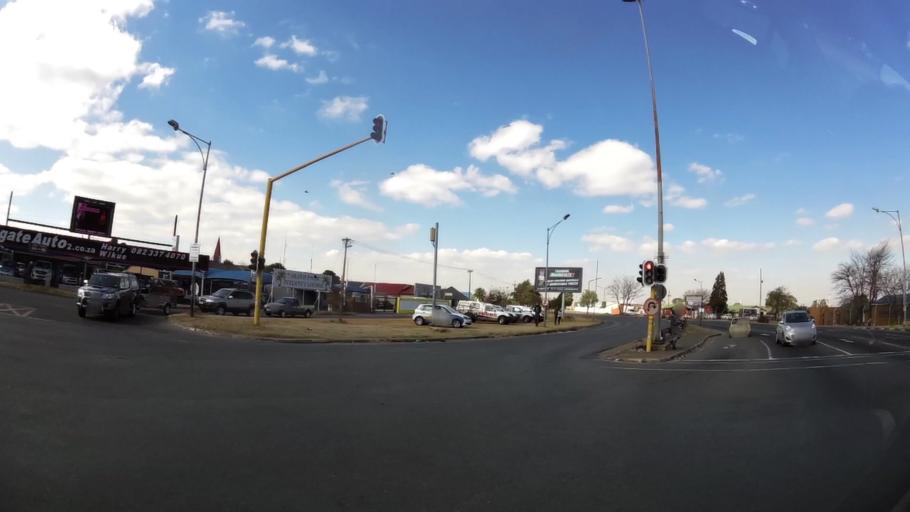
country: ZA
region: Gauteng
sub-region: West Rand District Municipality
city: Krugersdorp
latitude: -26.1199
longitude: 27.8180
